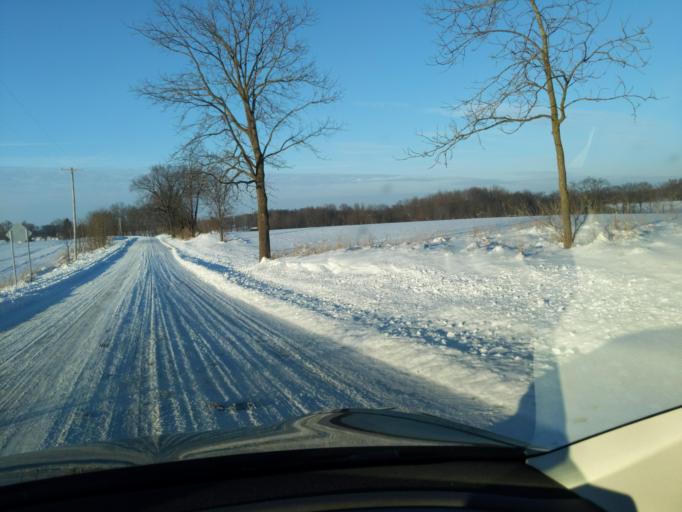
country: US
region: Michigan
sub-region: Ingham County
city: Stockbridge
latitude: 42.4991
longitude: -84.1191
